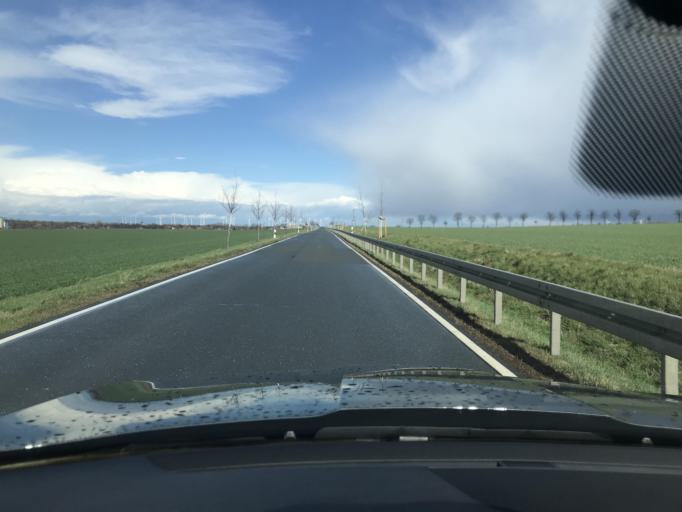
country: DE
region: Saxony-Anhalt
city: Hoym
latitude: 51.7197
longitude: 11.3169
